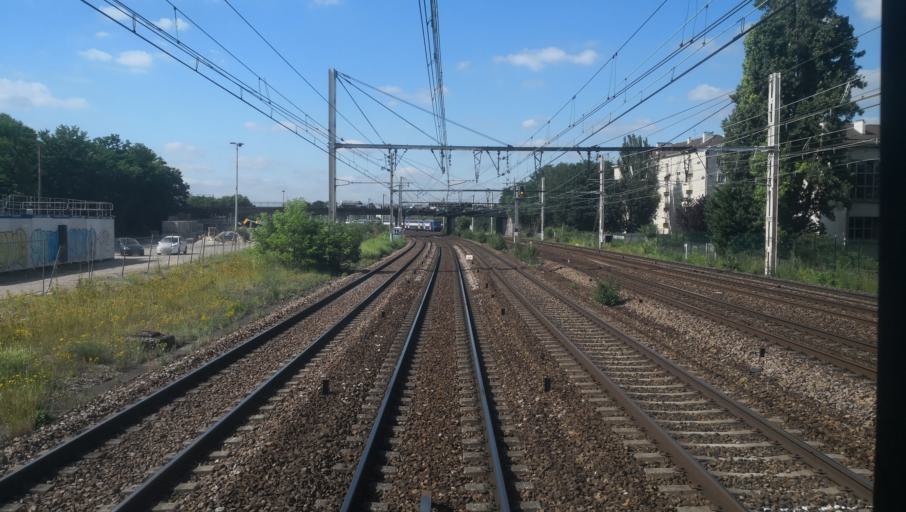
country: FR
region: Ile-de-France
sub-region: Departement du Val-de-Marne
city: Alfortville
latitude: 48.7949
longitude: 2.4301
